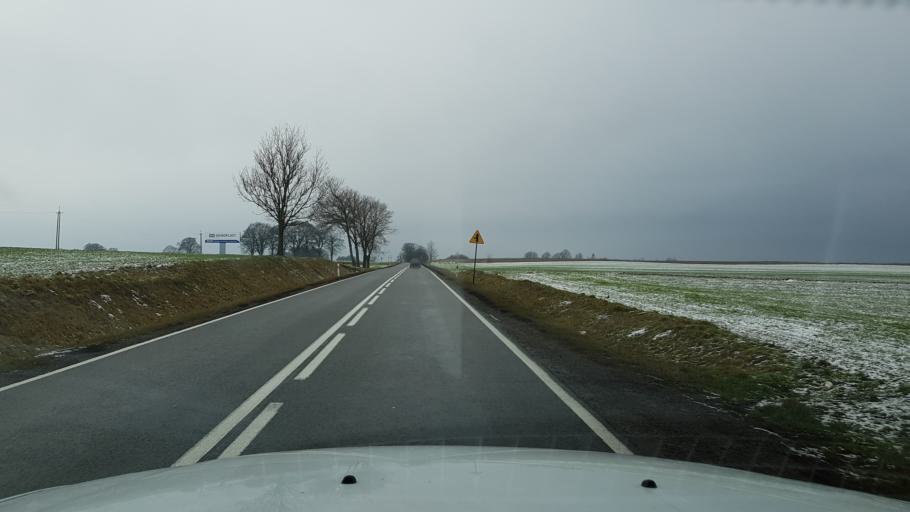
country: PL
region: West Pomeranian Voivodeship
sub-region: Powiat drawski
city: Czaplinek
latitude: 53.5557
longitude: 16.2196
